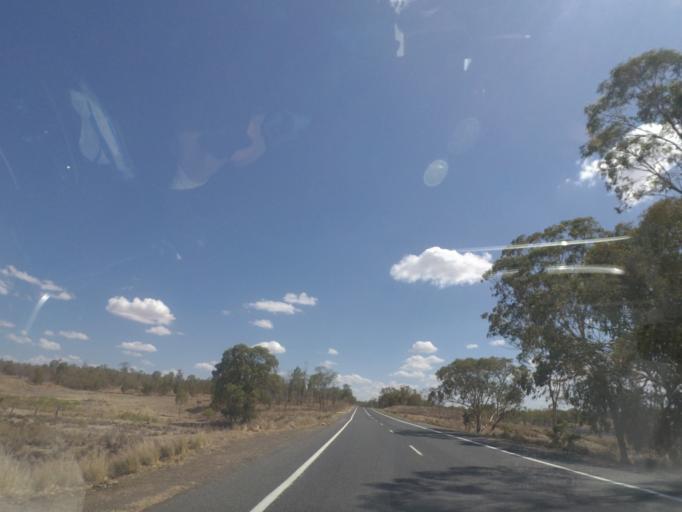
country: AU
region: Queensland
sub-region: Southern Downs
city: Warwick
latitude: -28.2237
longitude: 151.5530
